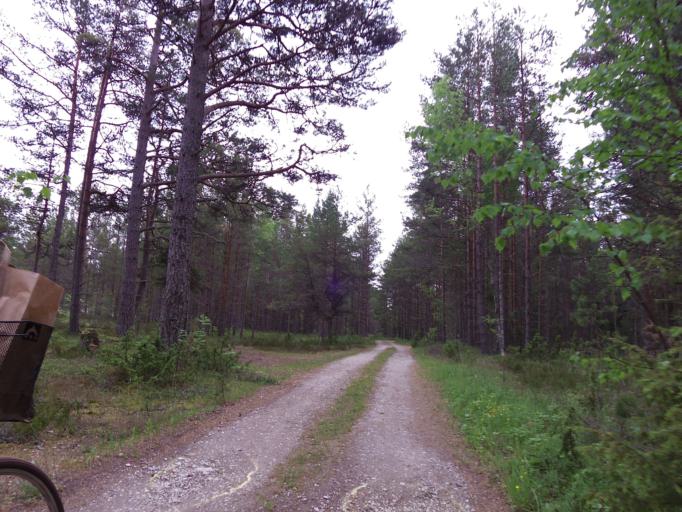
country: EE
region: Harju
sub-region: Paldiski linn
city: Paldiski
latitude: 59.2458
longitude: 23.7475
